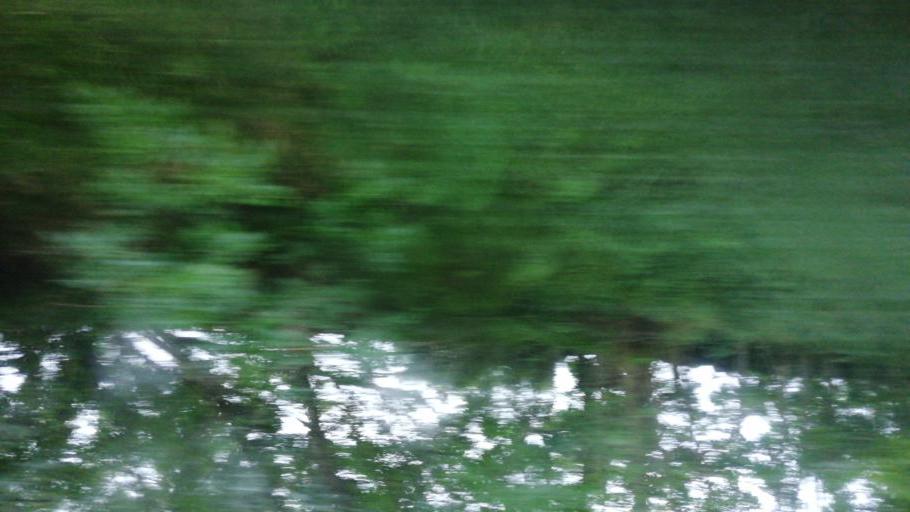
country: GB
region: Scotland
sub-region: Highland
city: Golspie
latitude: 57.9806
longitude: -3.9650
